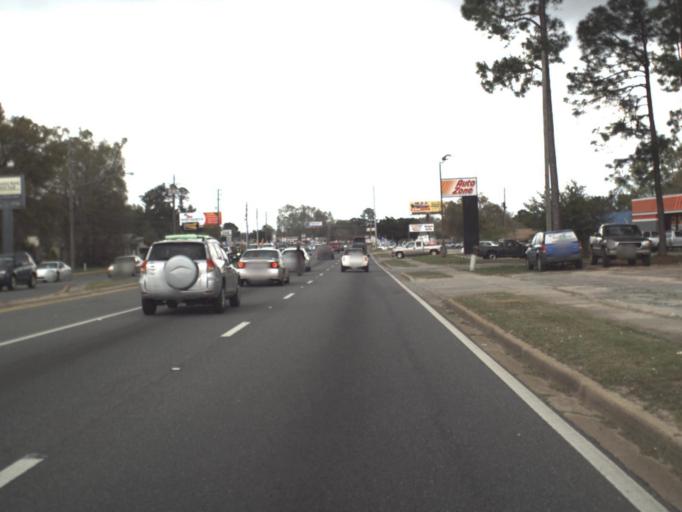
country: US
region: Florida
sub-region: Okaloosa County
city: Crestview
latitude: 30.7380
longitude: -86.5648
